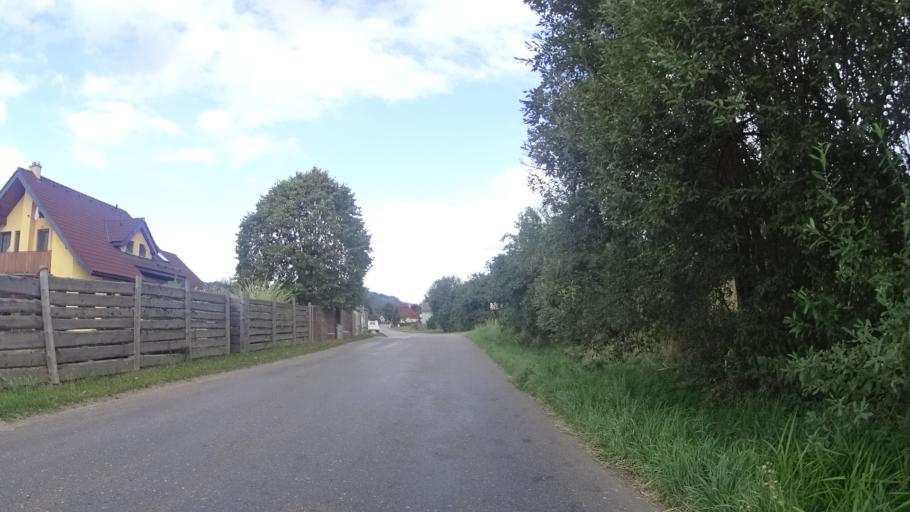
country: CZ
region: Pardubicky
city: Dolni Cermna
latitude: 49.9413
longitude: 16.5238
